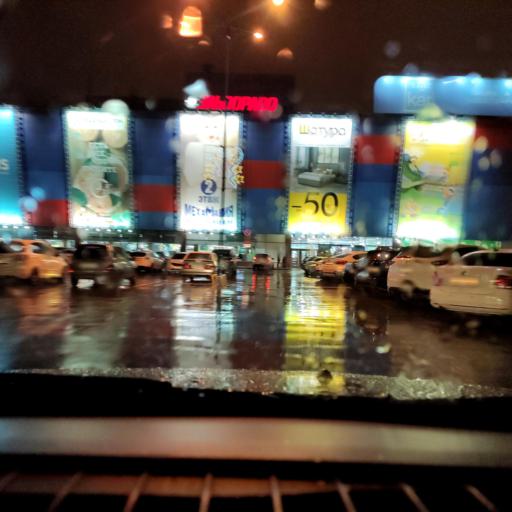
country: RU
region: Samara
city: Tol'yatti
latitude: 53.5179
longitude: 49.2701
